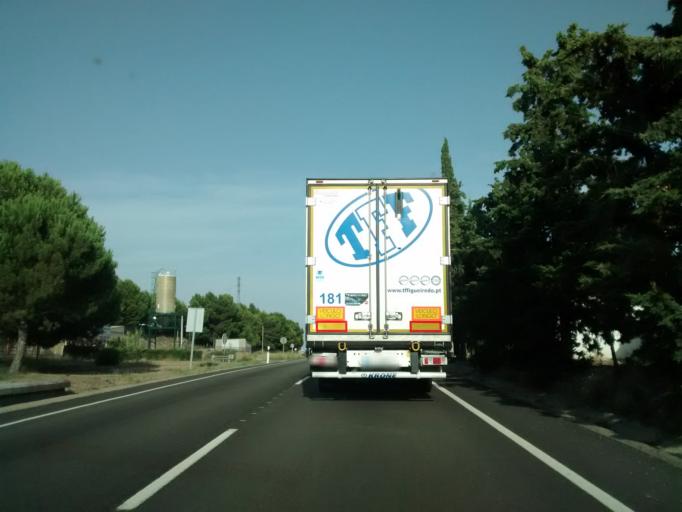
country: ES
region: Aragon
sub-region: Provincia de Zaragoza
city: Ainzon
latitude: 41.8315
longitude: -1.5169
